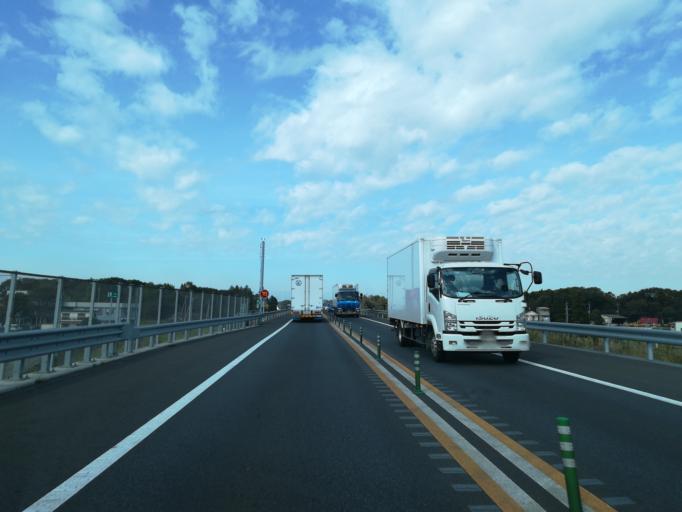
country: JP
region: Ibaraki
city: Iwai
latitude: 36.1026
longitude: 139.8649
